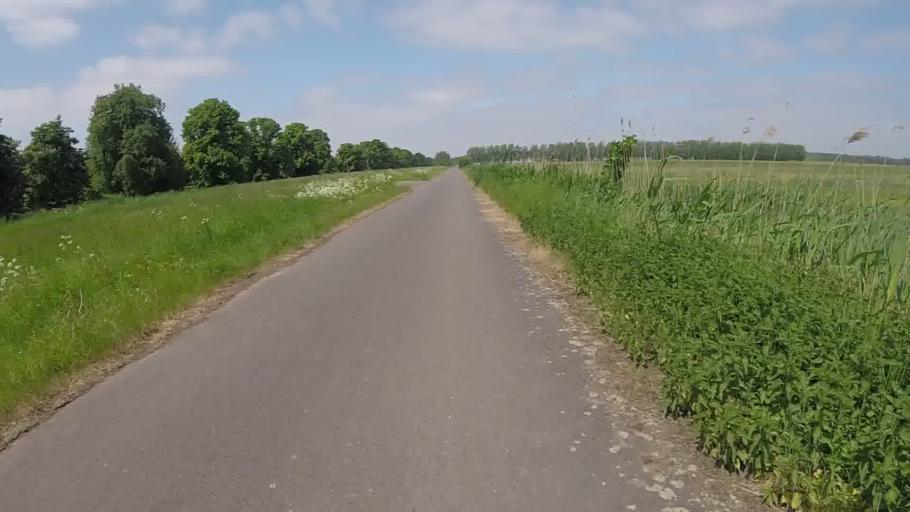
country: DE
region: Hamburg
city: Wandsbek
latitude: 53.5060
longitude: 10.1183
